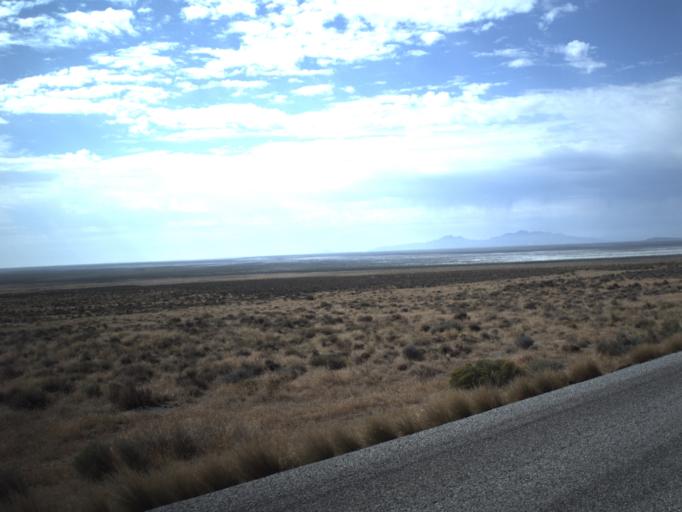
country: US
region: Utah
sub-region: Tooele County
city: Wendover
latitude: 41.4894
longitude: -113.6202
